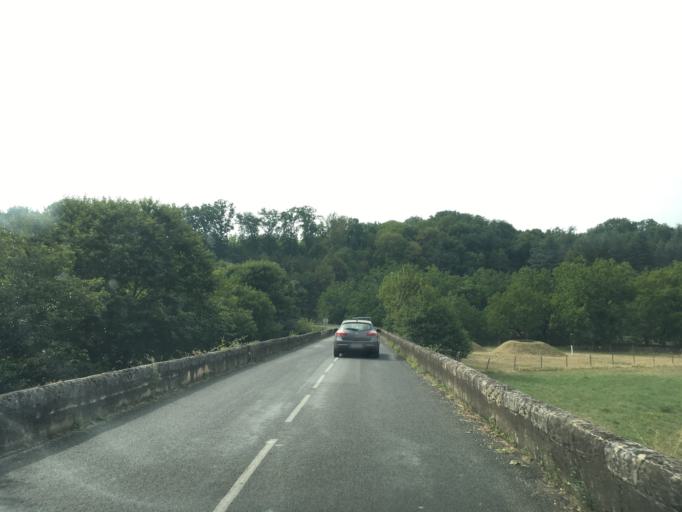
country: FR
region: Midi-Pyrenees
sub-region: Departement du Lot
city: Souillac
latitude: 44.8532
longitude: 1.5234
